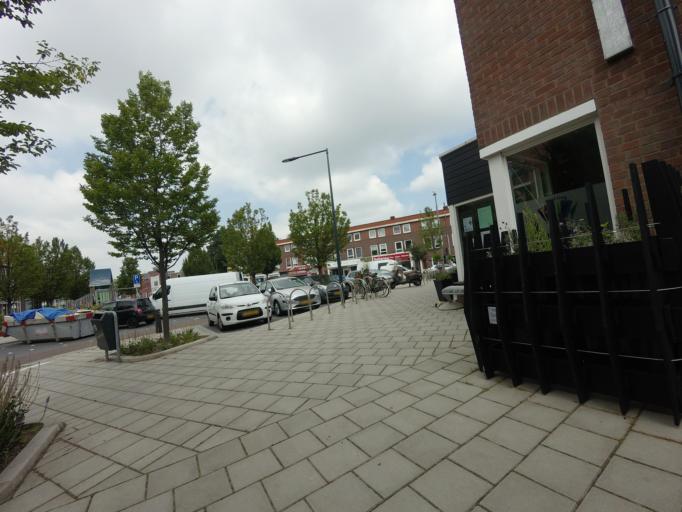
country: NL
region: South Holland
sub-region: Gemeente Schiedam
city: Schiedam
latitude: 51.9129
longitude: 4.3887
